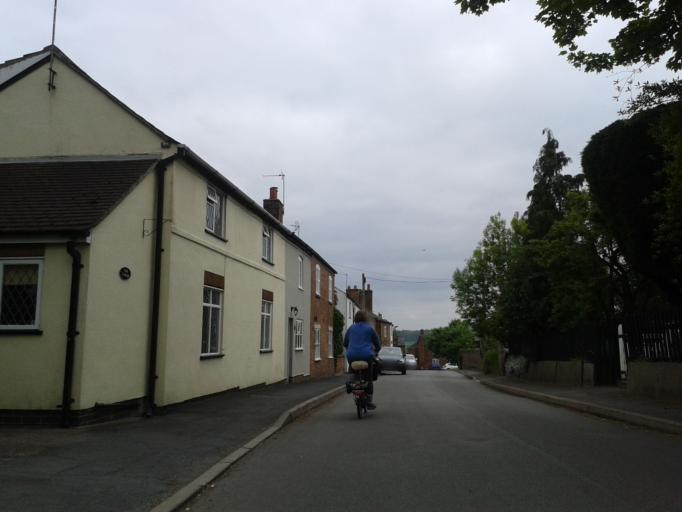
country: GB
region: England
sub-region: Leicestershire
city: Kibworth Harcourt
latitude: 52.5214
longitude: -1.0319
